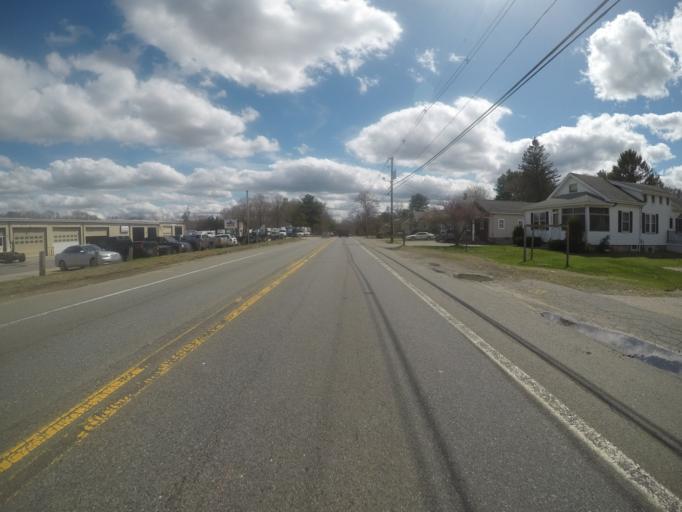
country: US
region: Massachusetts
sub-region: Bristol County
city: Raynham
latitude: 42.0013
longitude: -71.0669
